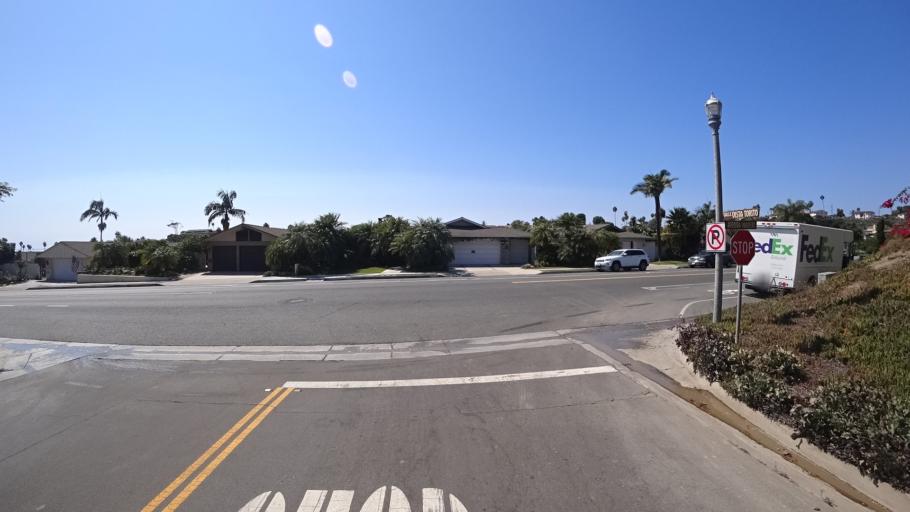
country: US
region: California
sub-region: Orange County
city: San Clemente
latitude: 33.4475
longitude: -117.6434
